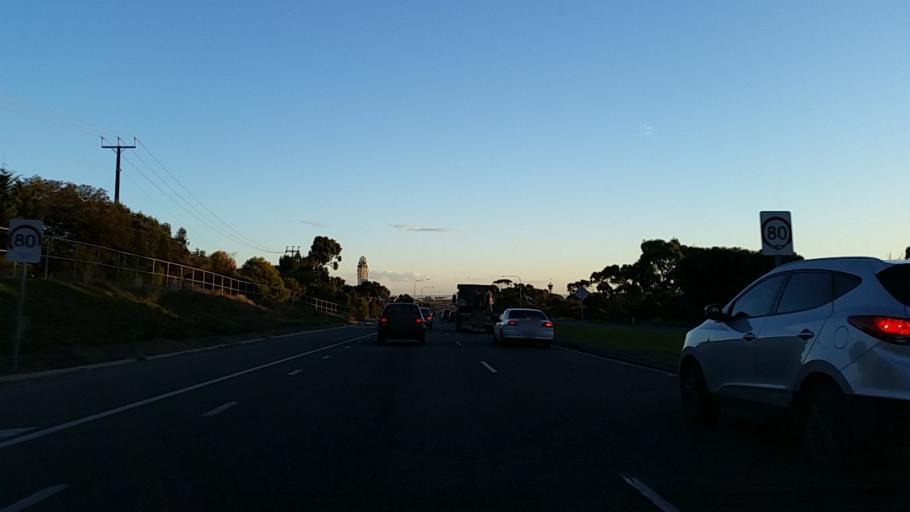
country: AU
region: South Australia
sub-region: Marion
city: Happy Valley
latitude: -35.0731
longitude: 138.5244
